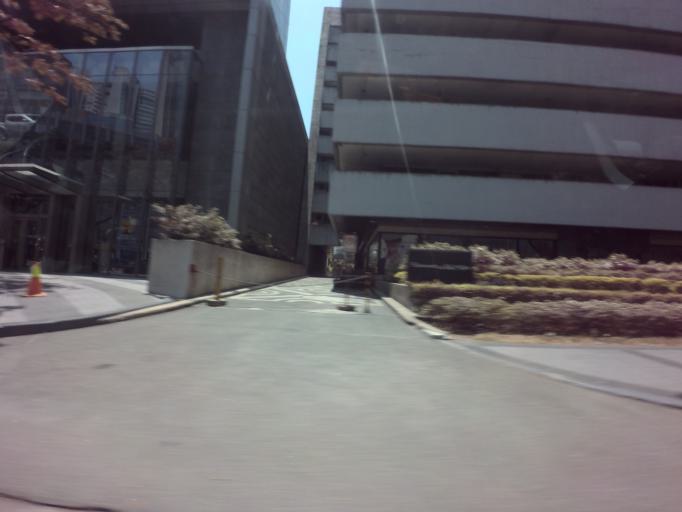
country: PH
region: Metro Manila
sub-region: Makati City
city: Makati City
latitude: 14.5577
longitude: 121.0260
